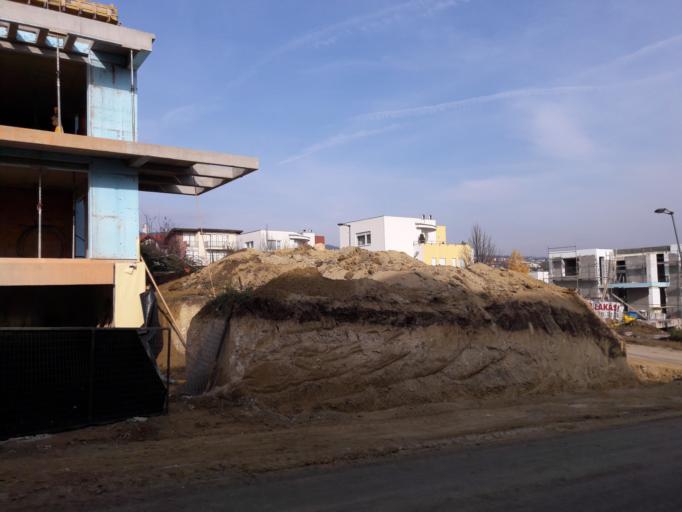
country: HU
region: Pest
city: Budaors
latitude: 47.4696
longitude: 18.9897
